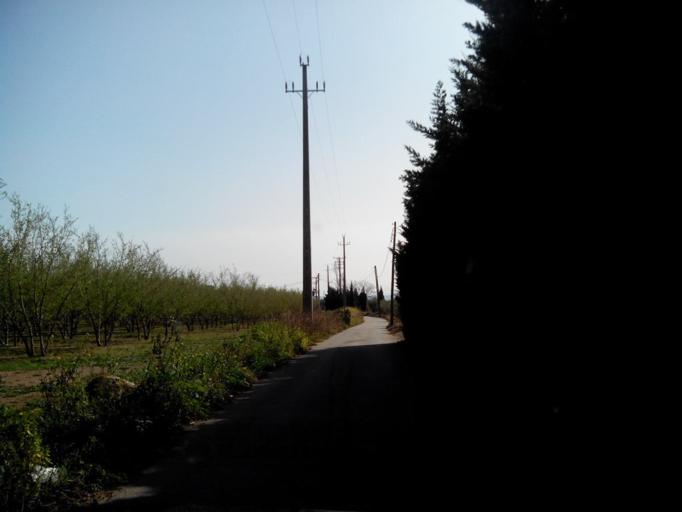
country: ES
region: Catalonia
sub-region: Provincia de Tarragona
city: La Selva
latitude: 41.2110
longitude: 1.1710
